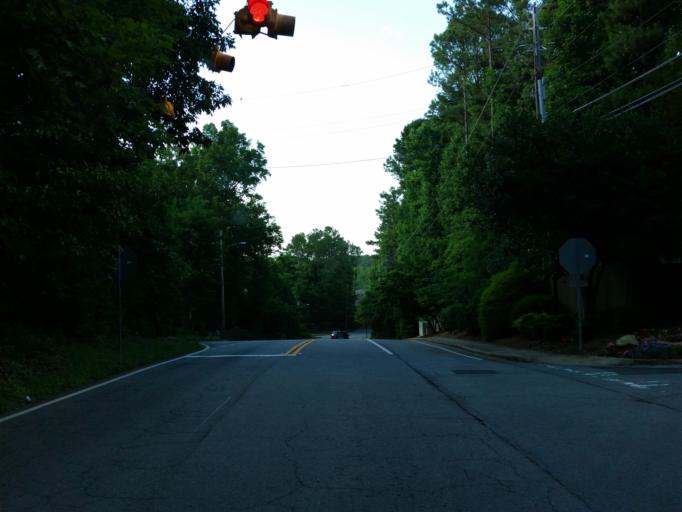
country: US
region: Georgia
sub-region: Cherokee County
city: Woodstock
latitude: 34.0532
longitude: -84.4760
